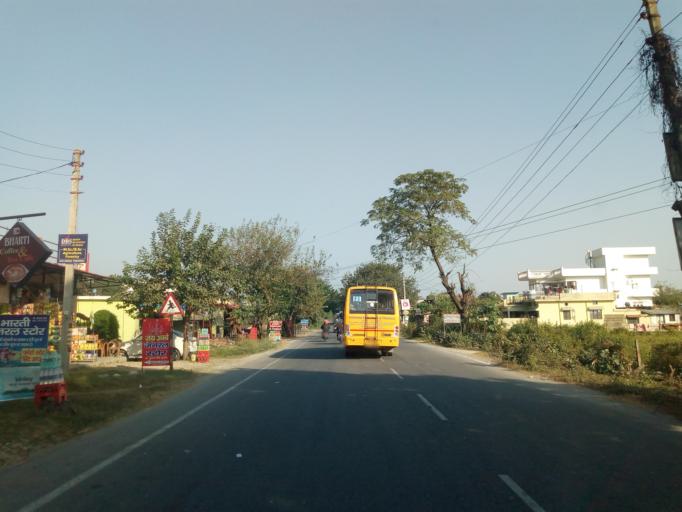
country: IN
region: Uttarakhand
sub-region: Dehradun
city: Dehradun
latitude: 30.3458
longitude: 77.9007
